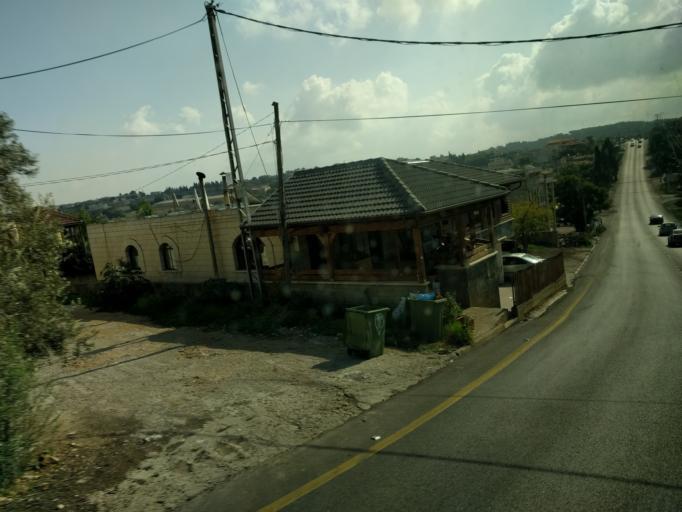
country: IL
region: Haifa
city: Daliyat el Karmil
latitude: 32.7138
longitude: 35.0682
